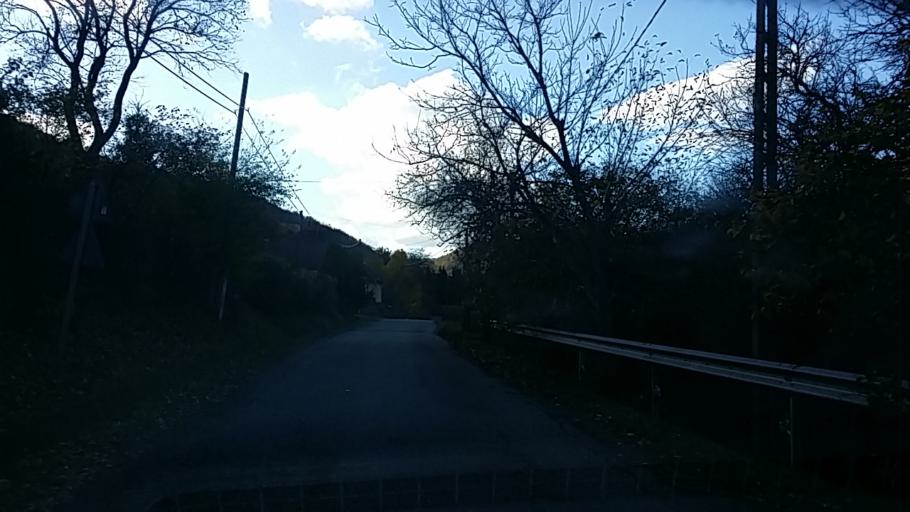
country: HU
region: Borsod-Abauj-Zemplen
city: Tolcsva
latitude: 48.3781
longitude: 21.4003
